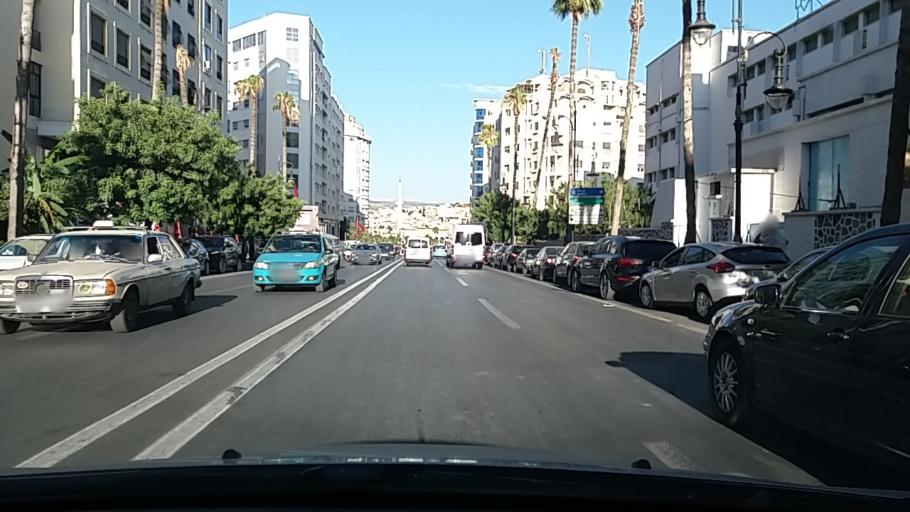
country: MA
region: Tanger-Tetouan
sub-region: Tanger-Assilah
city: Tangier
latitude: 35.7702
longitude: -5.8071
